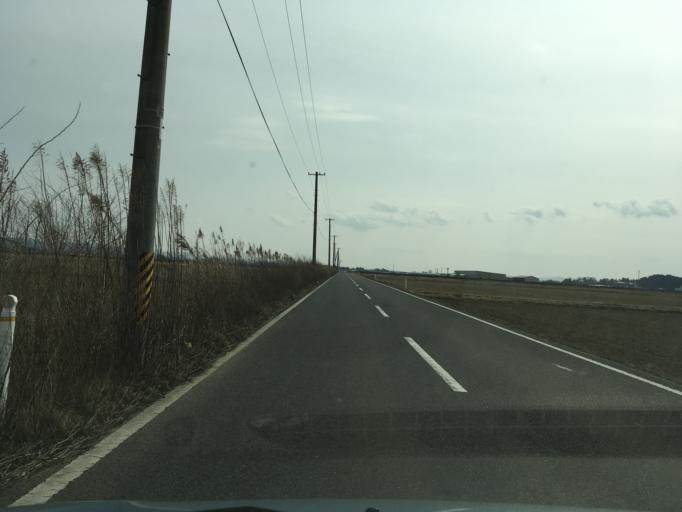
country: JP
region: Iwate
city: Ichinoseki
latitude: 38.7431
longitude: 141.2378
